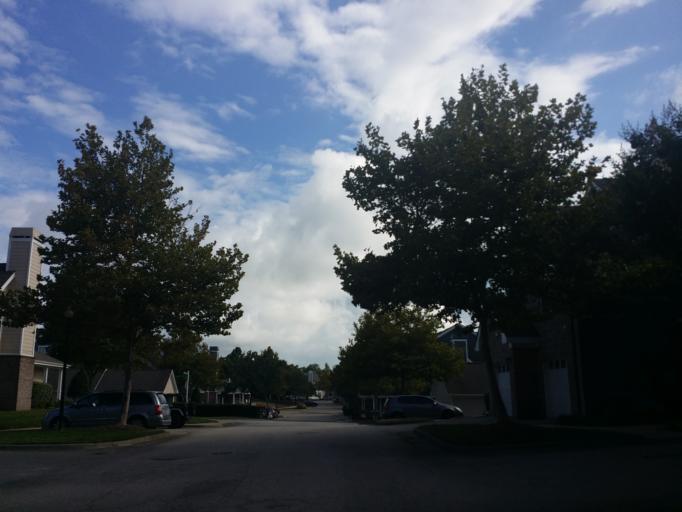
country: US
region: North Carolina
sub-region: Wake County
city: Morrisville
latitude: 35.9117
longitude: -78.7878
